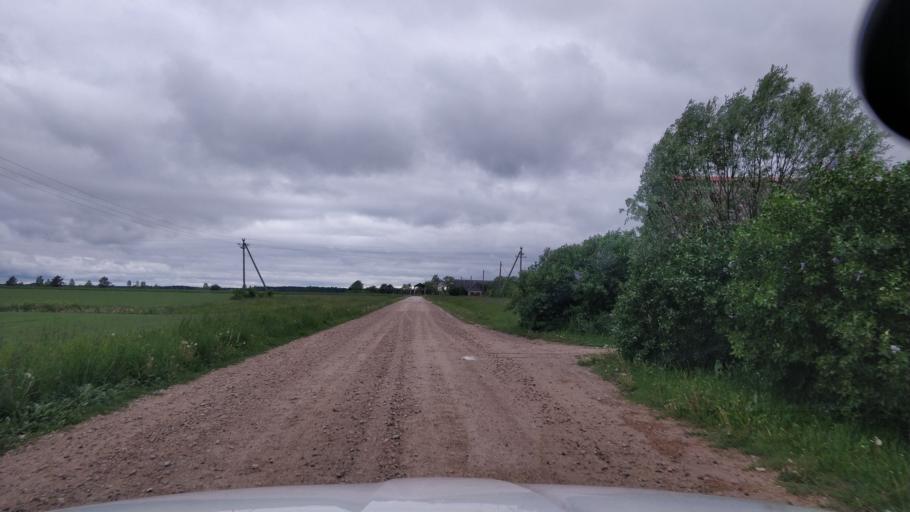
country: EE
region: Raplamaa
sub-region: Maerjamaa vald
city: Marjamaa
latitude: 58.7151
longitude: 24.2365
